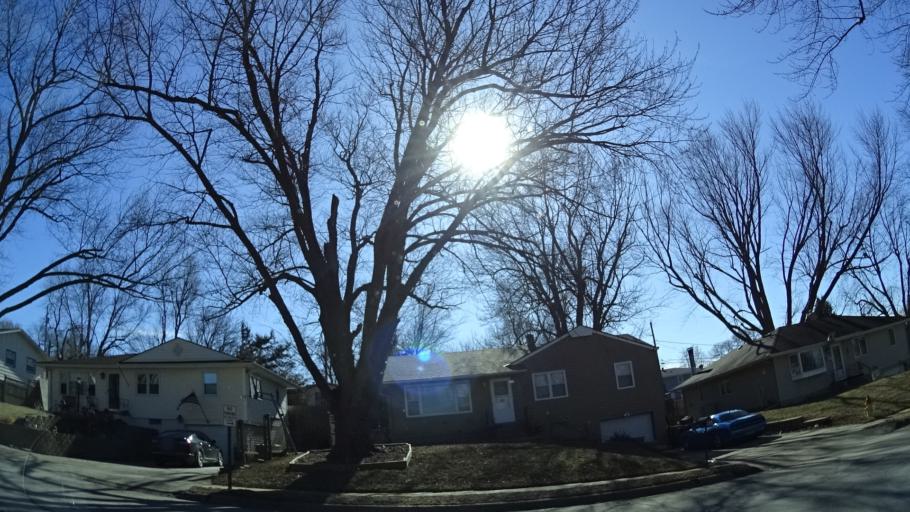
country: US
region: Nebraska
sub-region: Sarpy County
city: Offutt Air Force Base
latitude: 41.1381
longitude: -95.9188
